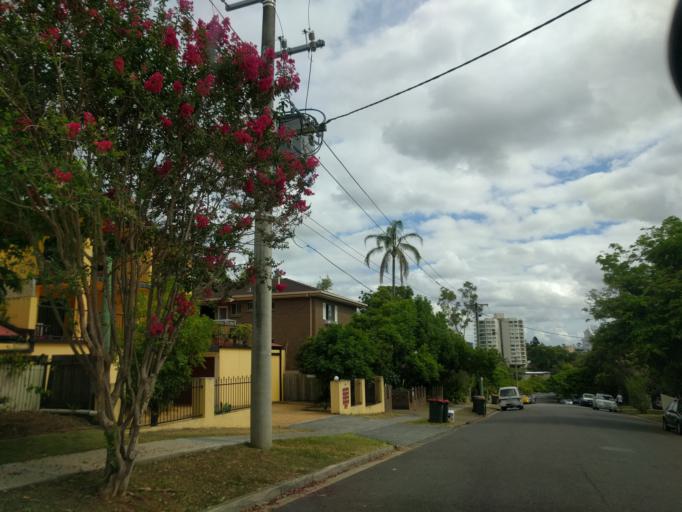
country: AU
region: Queensland
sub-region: Brisbane
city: Toowong
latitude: -27.4963
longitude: 153.0036
